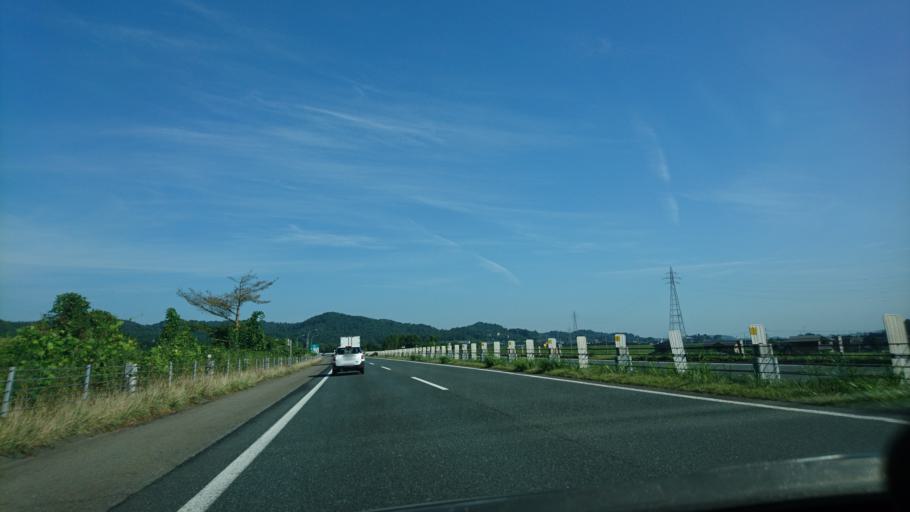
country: JP
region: Iwate
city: Ichinoseki
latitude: 38.9771
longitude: 141.1108
